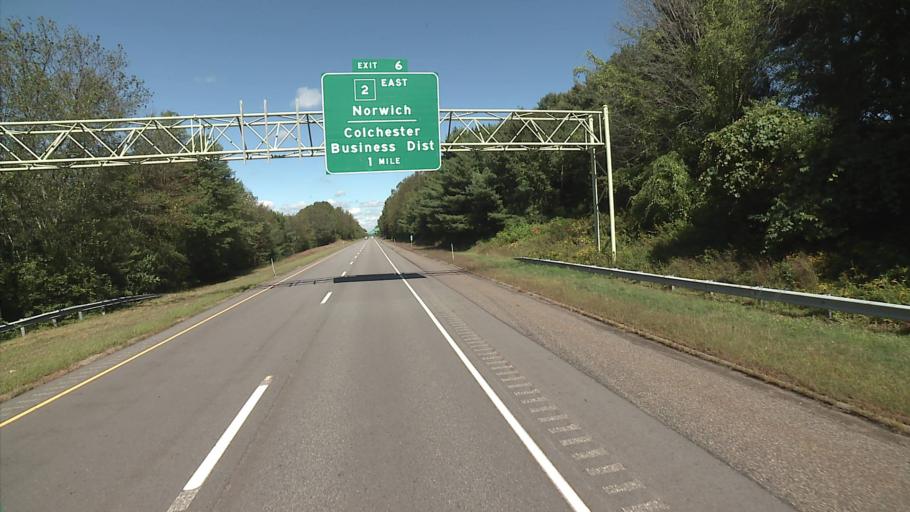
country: US
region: Connecticut
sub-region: New London County
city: Colchester
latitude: 41.5416
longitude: -72.3135
